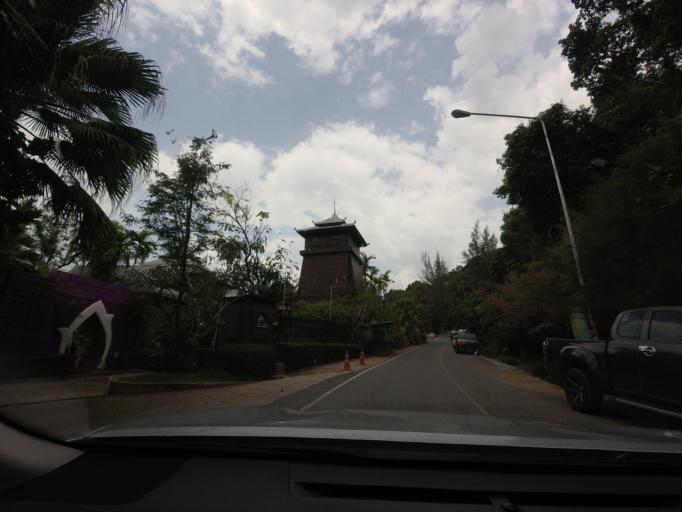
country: TH
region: Phangnga
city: Ban Ao Nang
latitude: 8.0931
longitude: 98.7485
